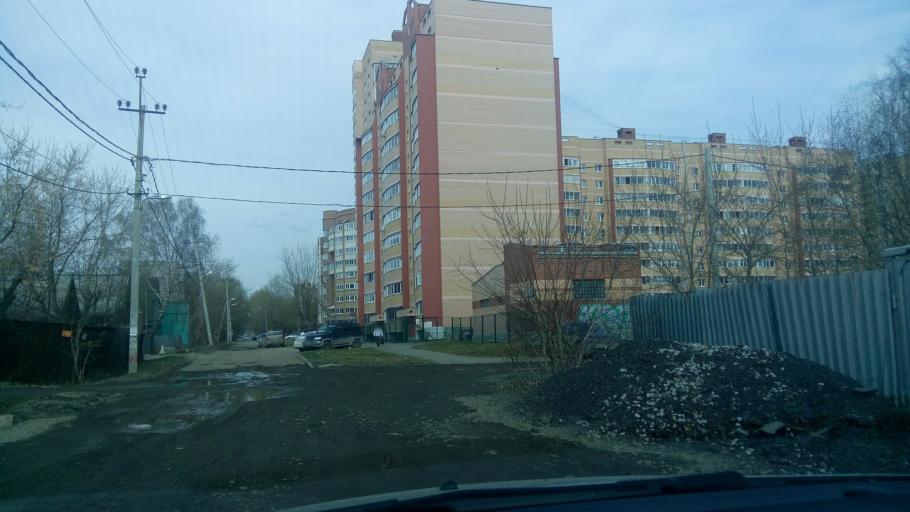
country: RU
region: Sverdlovsk
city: Yekaterinburg
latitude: 56.9078
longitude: 60.5856
